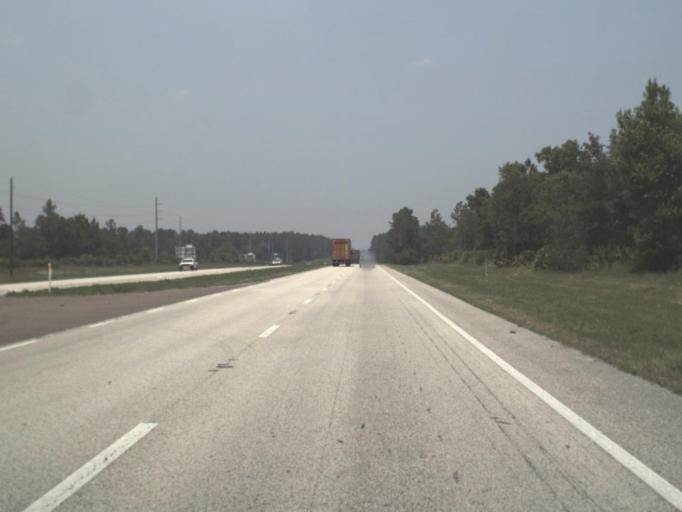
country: US
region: Florida
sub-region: Baker County
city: Macclenny
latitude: 30.1373
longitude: -82.0381
